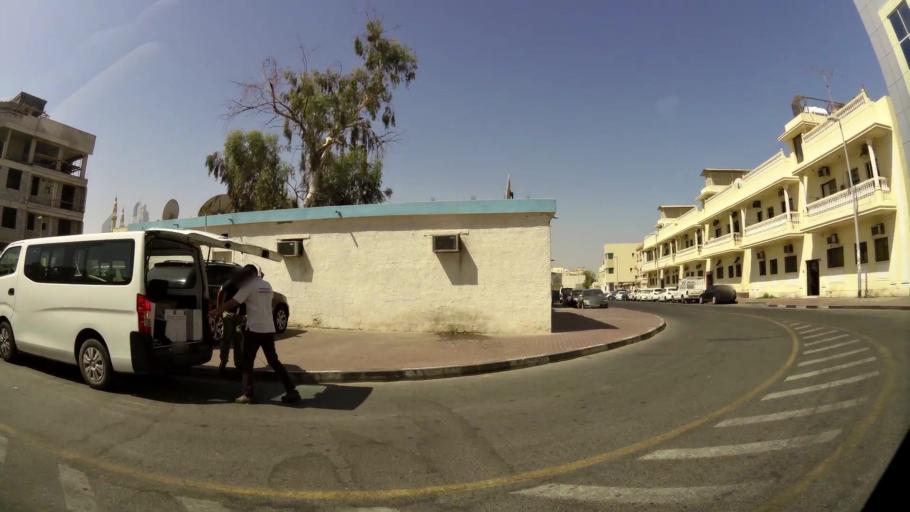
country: AE
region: Ash Shariqah
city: Sharjah
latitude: 25.2346
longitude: 55.2761
